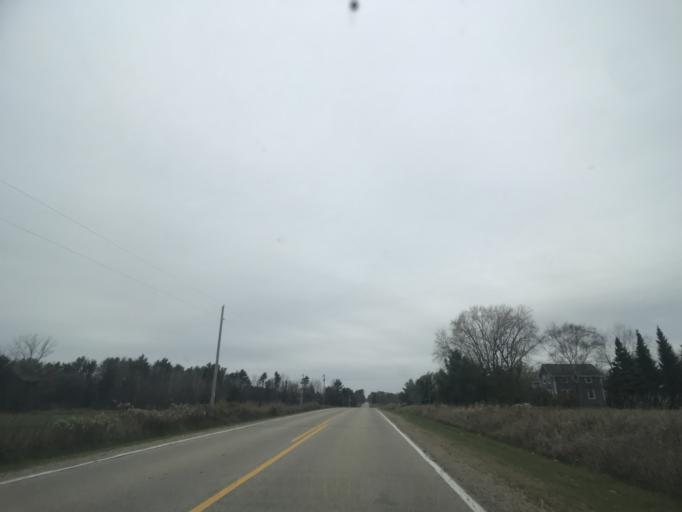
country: US
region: Wisconsin
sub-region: Oconto County
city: Gillett
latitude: 44.9836
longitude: -88.3117
